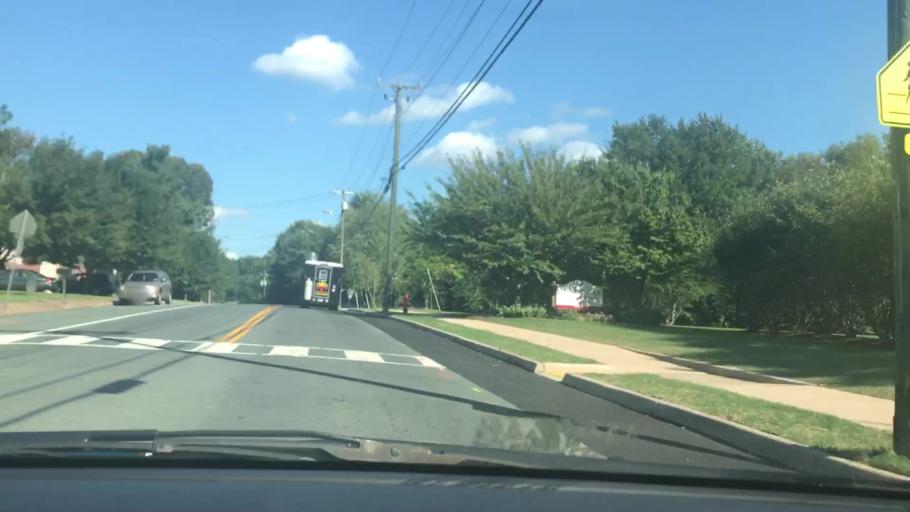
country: US
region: Virginia
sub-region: City of Charlottesville
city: Charlottesville
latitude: 38.0151
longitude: -78.5038
